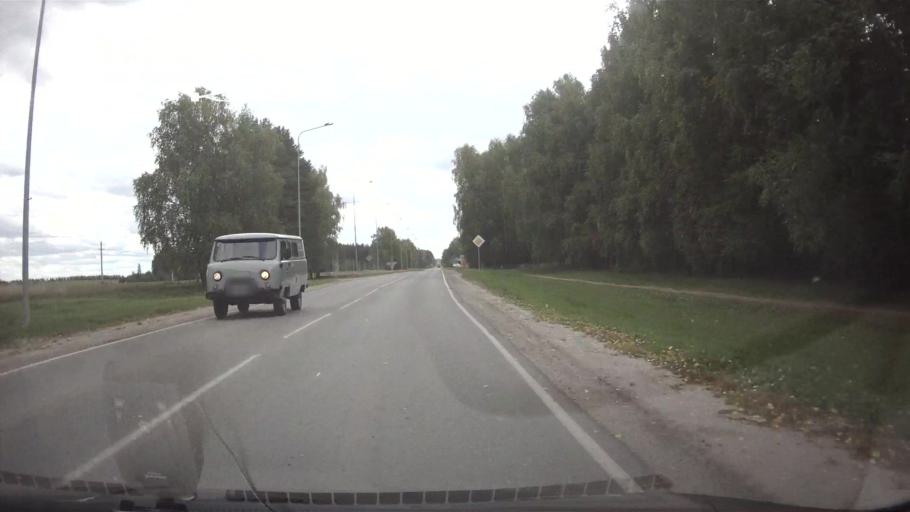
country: RU
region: Mariy-El
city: Kuzhener
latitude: 56.9962
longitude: 48.7423
